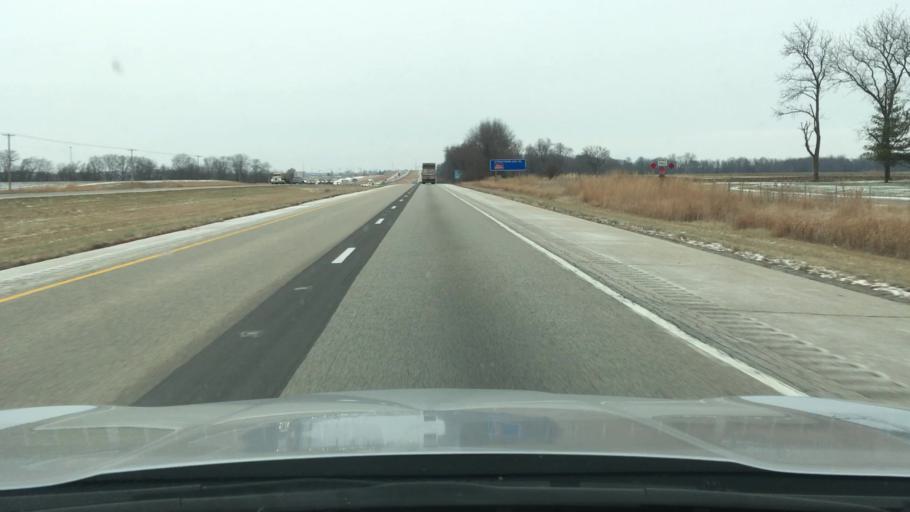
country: US
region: Illinois
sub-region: Sangamon County
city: Divernon
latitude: 39.5745
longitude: -89.6461
